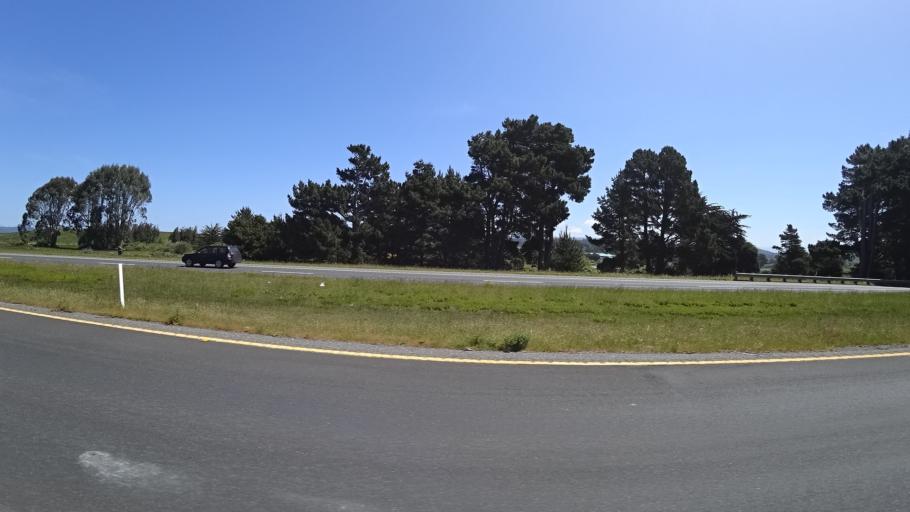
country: US
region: California
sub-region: Humboldt County
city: McKinleyville
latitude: 40.9698
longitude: -124.1162
